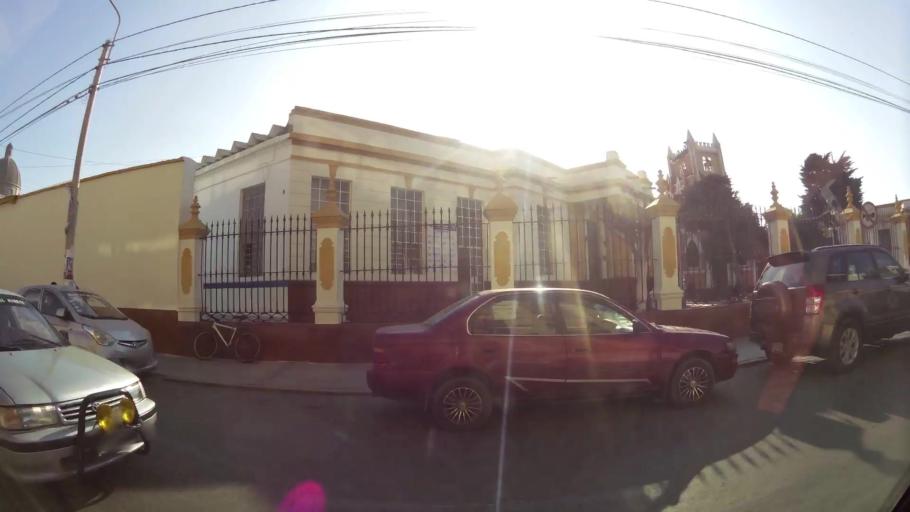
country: PE
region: Lambayeque
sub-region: Provincia de Chiclayo
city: Chiclayo
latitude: -6.7727
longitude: -79.8424
